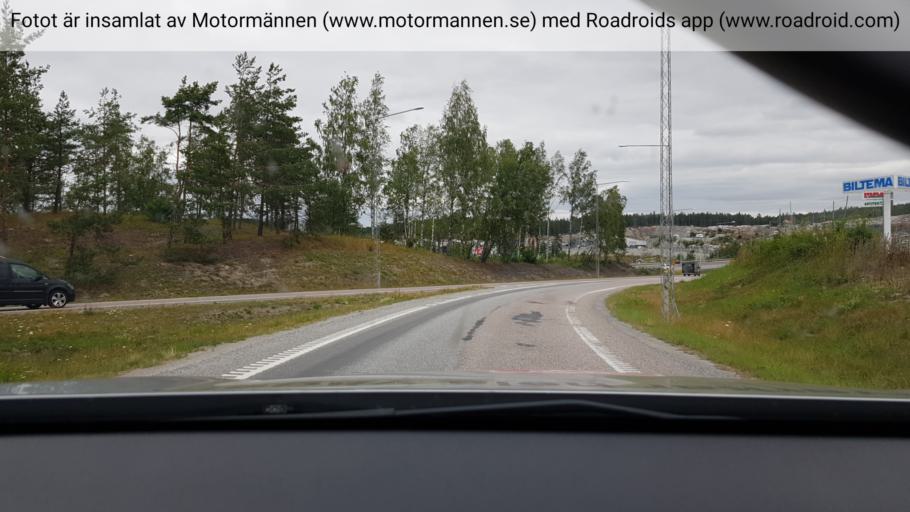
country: SE
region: Stockholm
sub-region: Sodertalje Kommun
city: Soedertaelje
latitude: 59.1995
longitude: 17.6664
